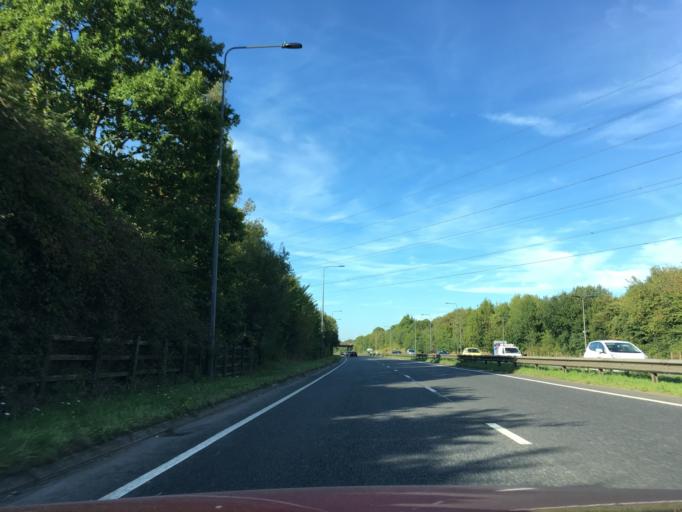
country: GB
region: England
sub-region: South Gloucestershire
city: Siston
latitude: 51.4781
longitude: -2.4752
